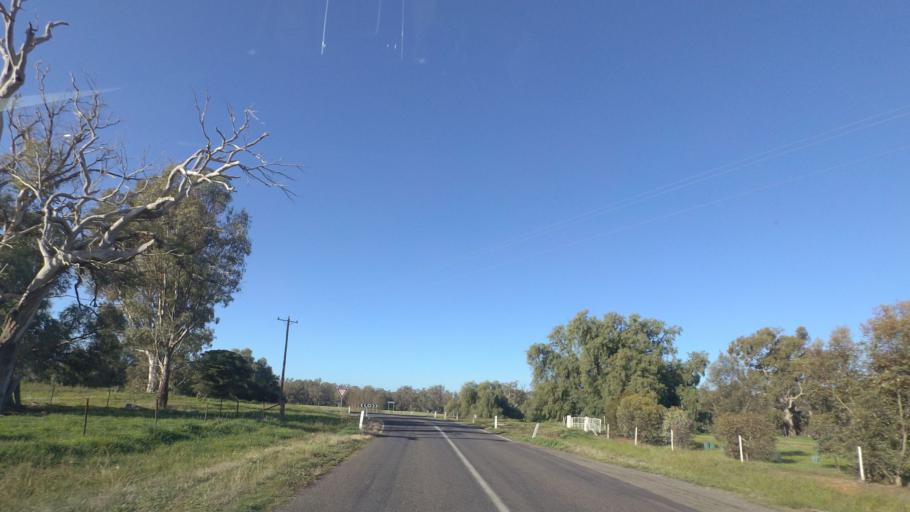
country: AU
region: Victoria
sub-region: Greater Bendigo
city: Epsom
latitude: -36.6465
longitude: 144.5396
